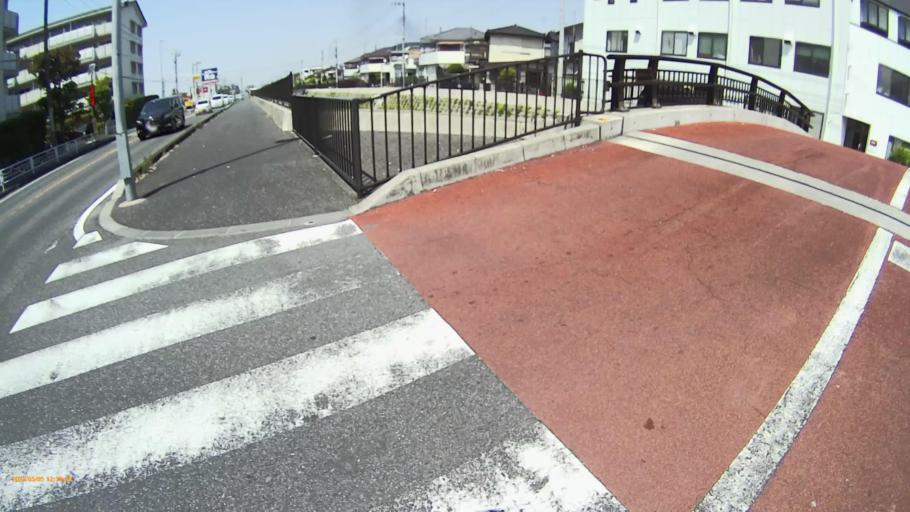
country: JP
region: Saitama
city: Kasukabe
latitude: 35.9391
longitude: 139.7770
